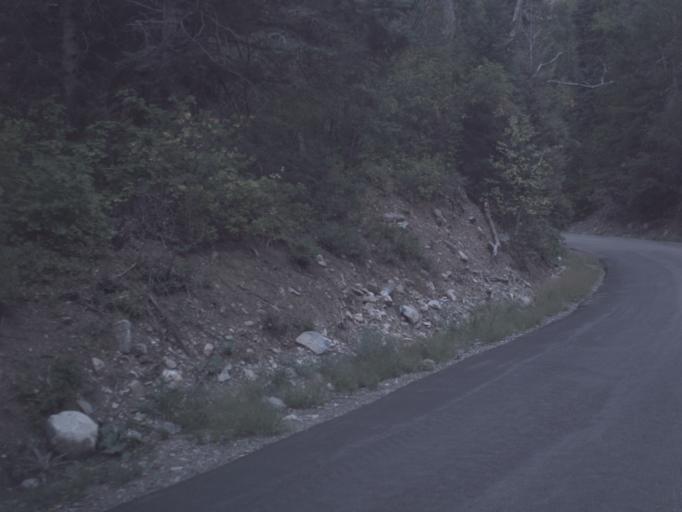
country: US
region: Utah
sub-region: Utah County
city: Cedar Hills
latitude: 40.4460
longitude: -111.6406
